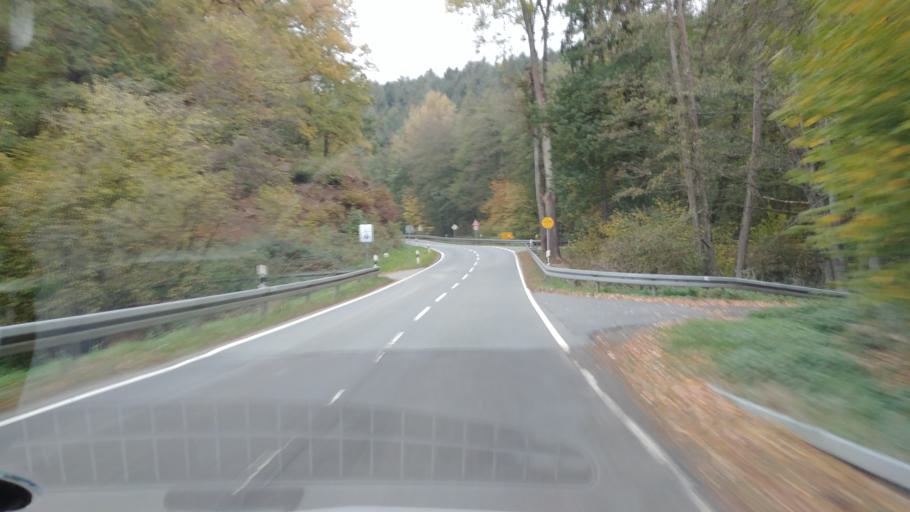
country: DE
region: Hesse
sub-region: Regierungsbezirk Darmstadt
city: Idstein
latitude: 50.2486
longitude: 8.2348
